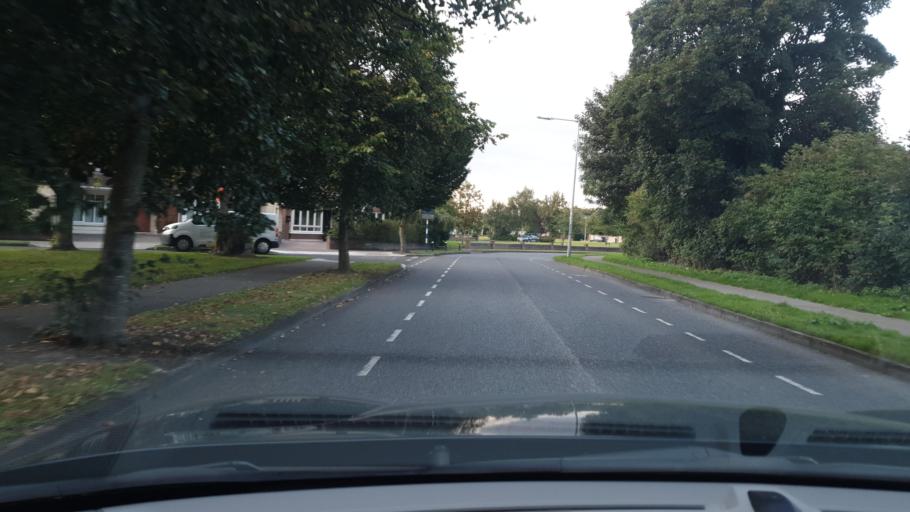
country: IE
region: Leinster
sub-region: Kildare
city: Sallins
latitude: 53.2347
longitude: -6.6518
